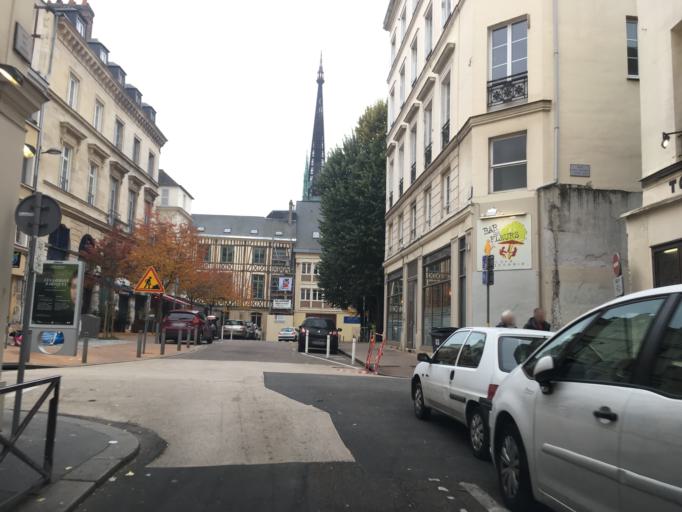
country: FR
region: Haute-Normandie
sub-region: Departement de la Seine-Maritime
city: Rouen
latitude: 49.4426
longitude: 1.0966
